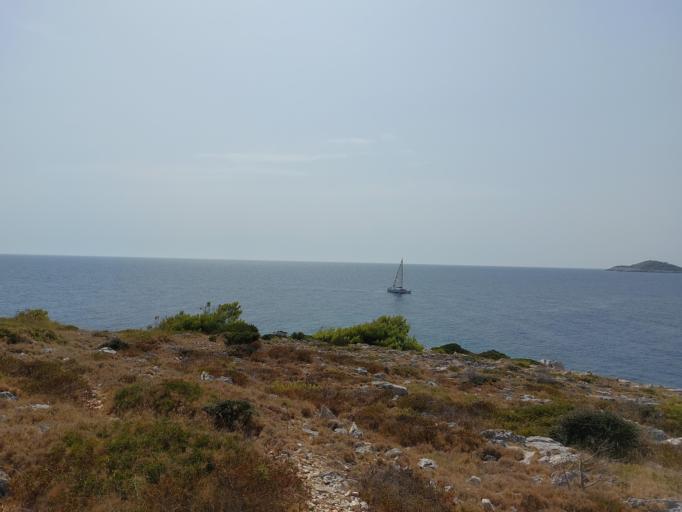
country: HR
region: Dubrovacko-Neretvanska
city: Smokvica
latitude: 42.7254
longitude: 16.8817
